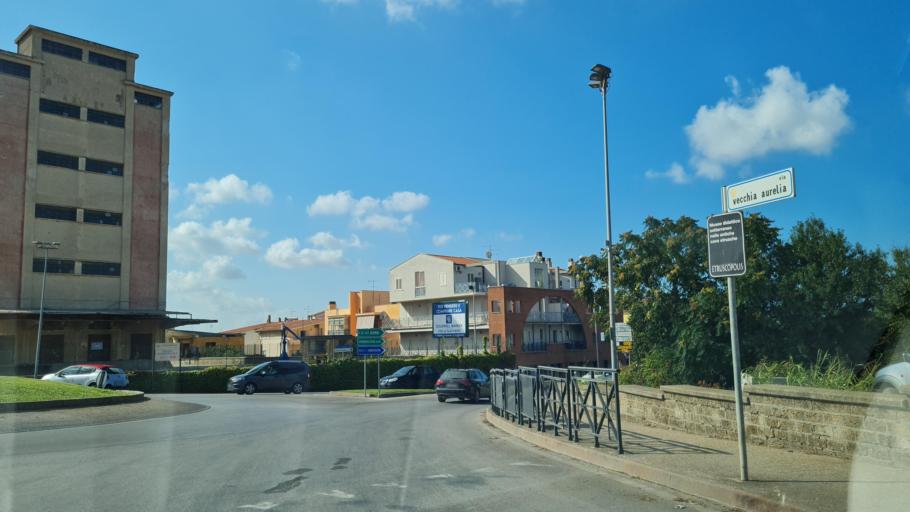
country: IT
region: Latium
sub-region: Provincia di Viterbo
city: Tarquinia
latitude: 42.2493
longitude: 11.7522
